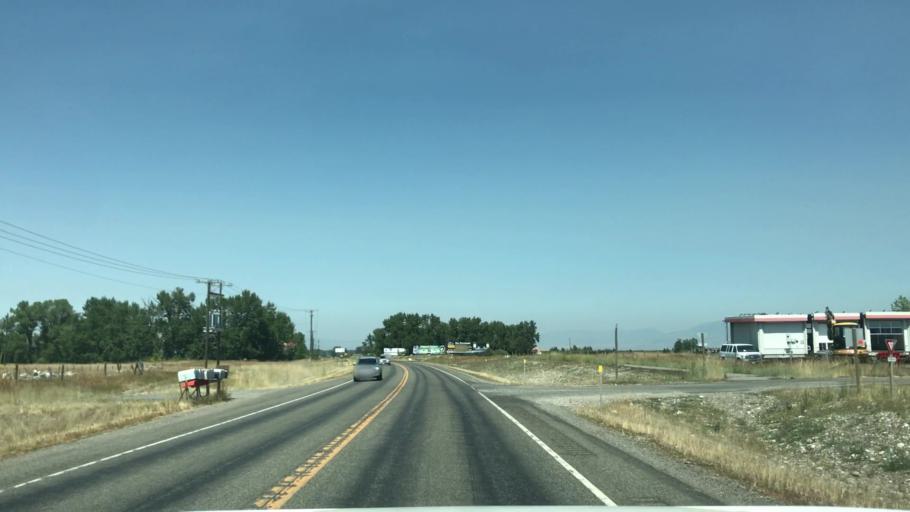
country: US
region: Montana
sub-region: Gallatin County
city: Four Corners
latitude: 45.6070
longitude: -111.1958
